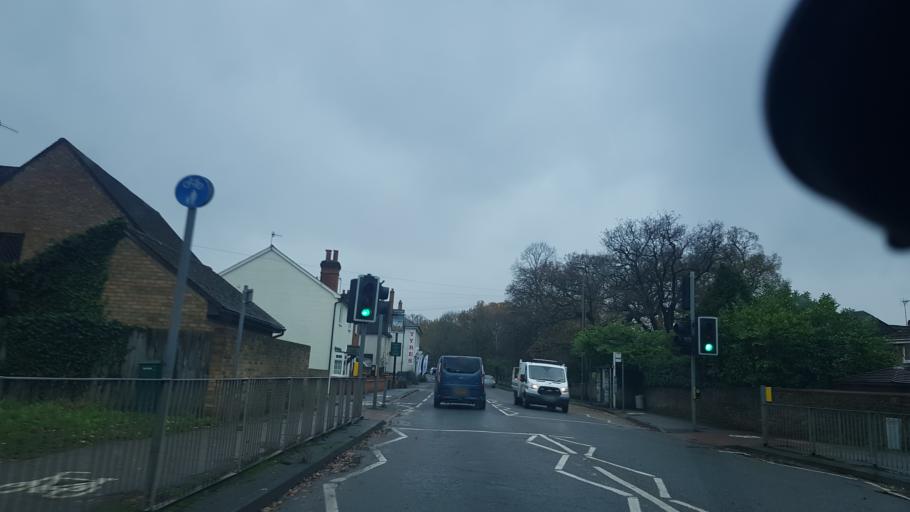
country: GB
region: England
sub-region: Surrey
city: Guildford
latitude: 51.2555
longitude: -0.5483
